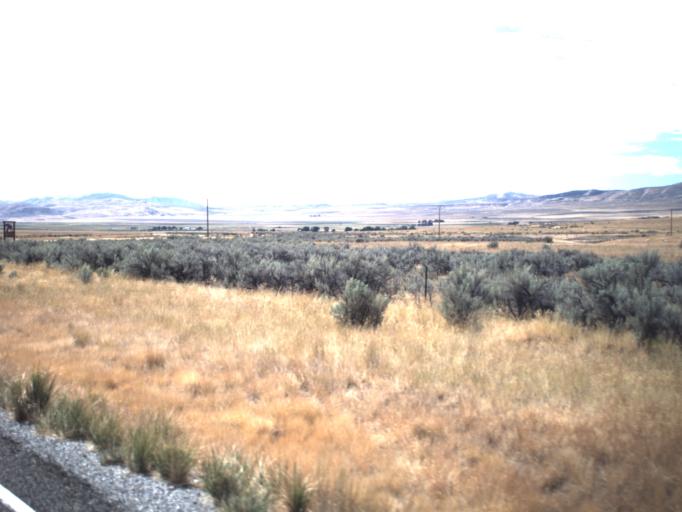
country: US
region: Utah
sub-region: Box Elder County
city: Garland
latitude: 41.7973
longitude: -112.4162
